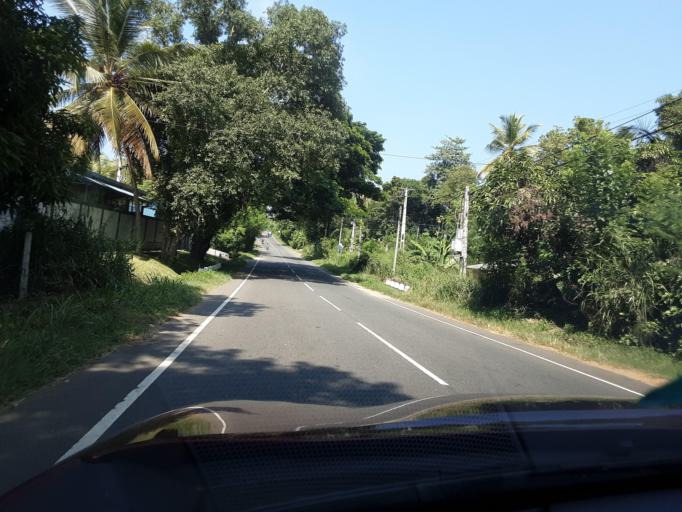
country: LK
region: Uva
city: Badulla
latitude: 7.1870
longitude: 81.0388
